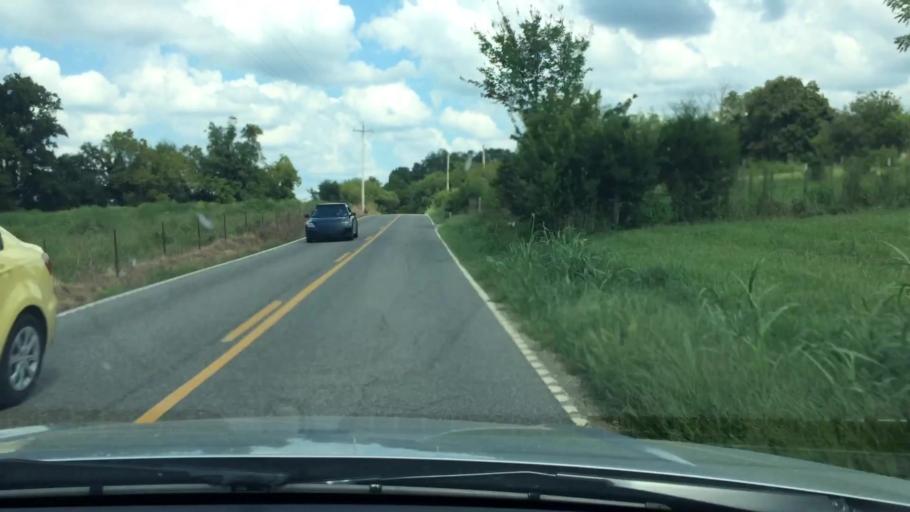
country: US
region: Tennessee
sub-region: McMinn County
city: Englewood
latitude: 35.5049
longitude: -84.4871
